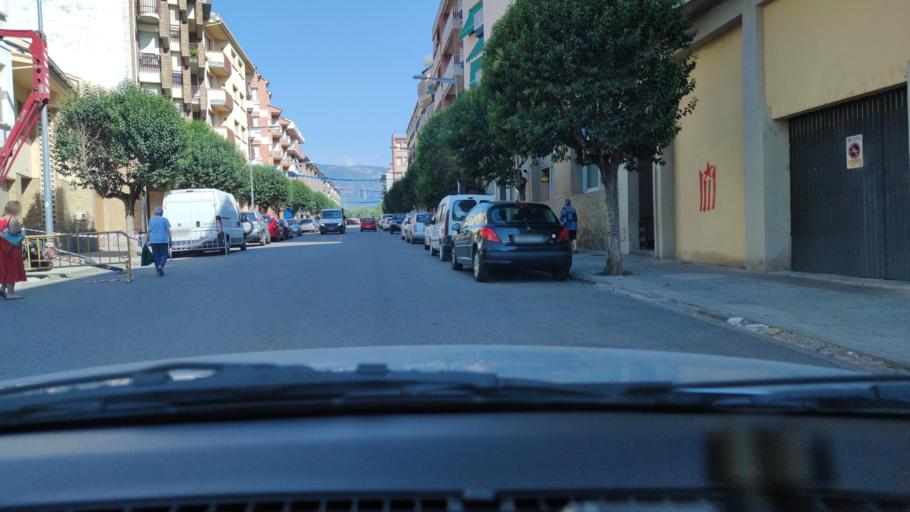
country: ES
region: Catalonia
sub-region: Provincia de Lleida
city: Senterada
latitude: 42.2491
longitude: 0.9660
